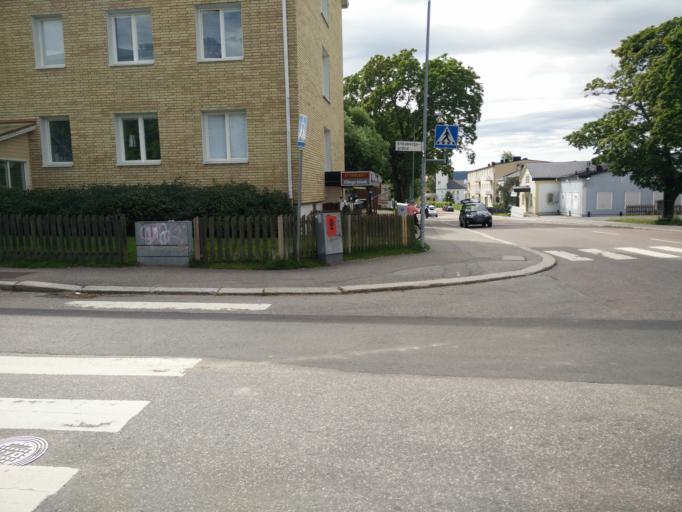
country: SE
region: Vaesternorrland
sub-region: Haernoesands Kommun
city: Haernoesand
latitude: 62.6355
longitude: 17.9484
